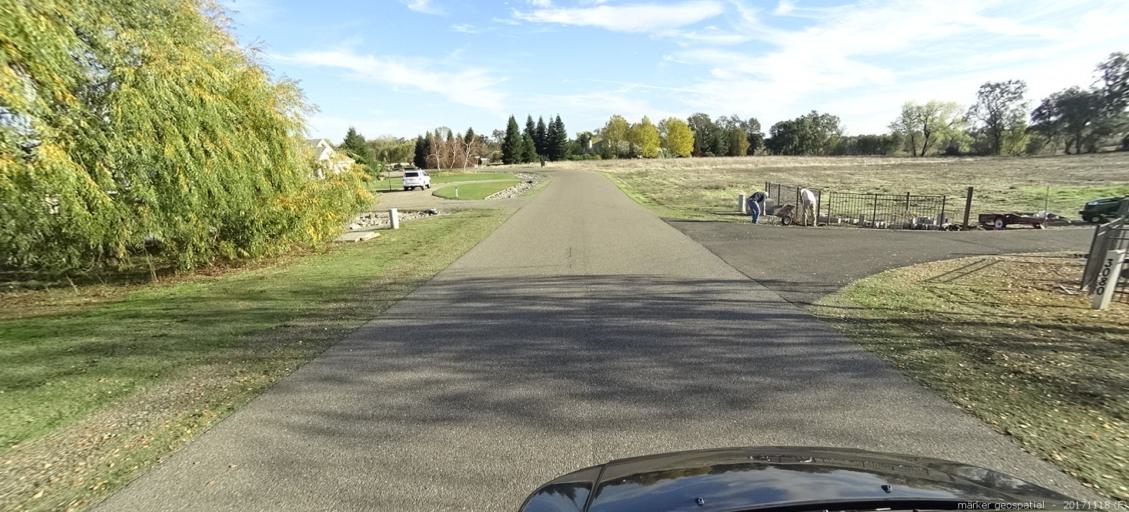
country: US
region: California
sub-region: Shasta County
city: Cottonwood
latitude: 40.3761
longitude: -122.3345
